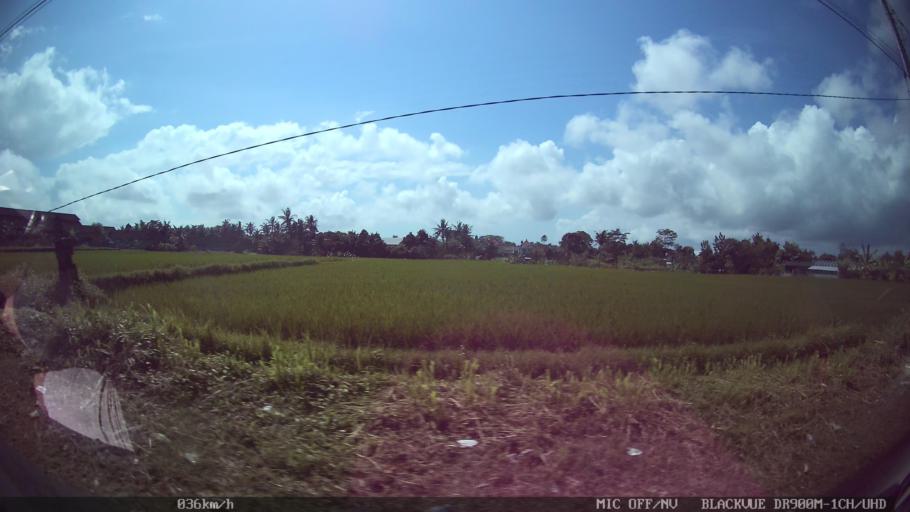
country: ID
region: Bali
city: Banjar Sedang
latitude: -8.5545
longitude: 115.2689
